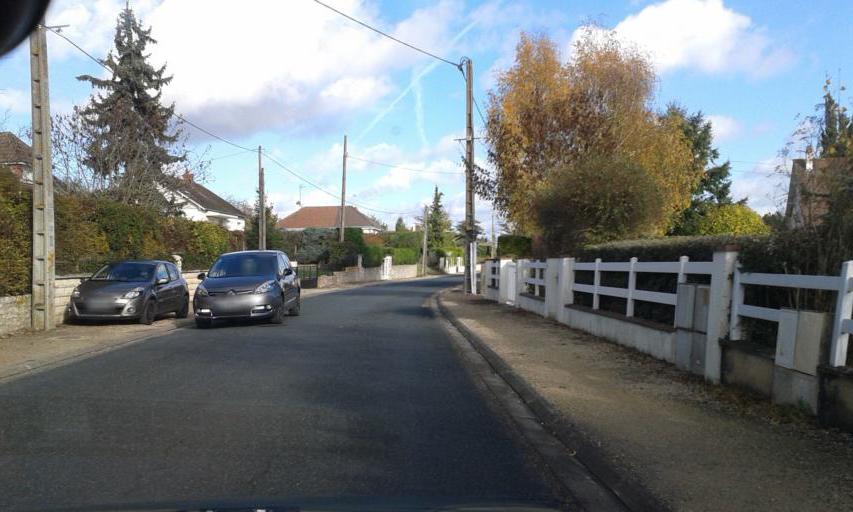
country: FR
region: Centre
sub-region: Departement du Loiret
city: Tavers
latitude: 47.7646
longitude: 1.6244
